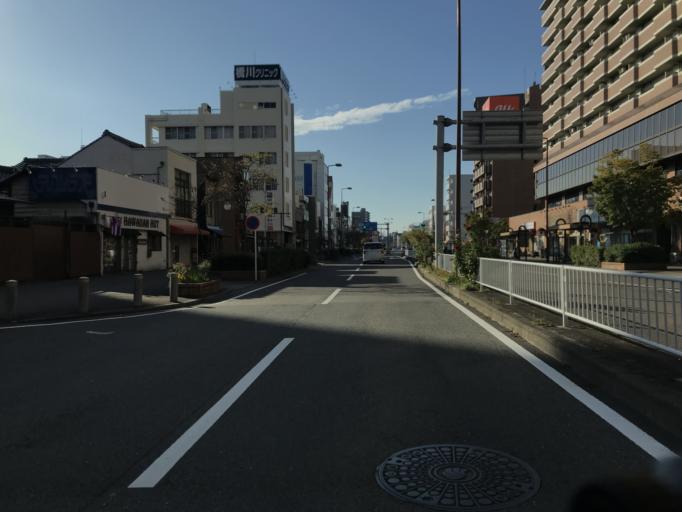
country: JP
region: Aichi
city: Nagoya-shi
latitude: 35.1921
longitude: 136.8900
